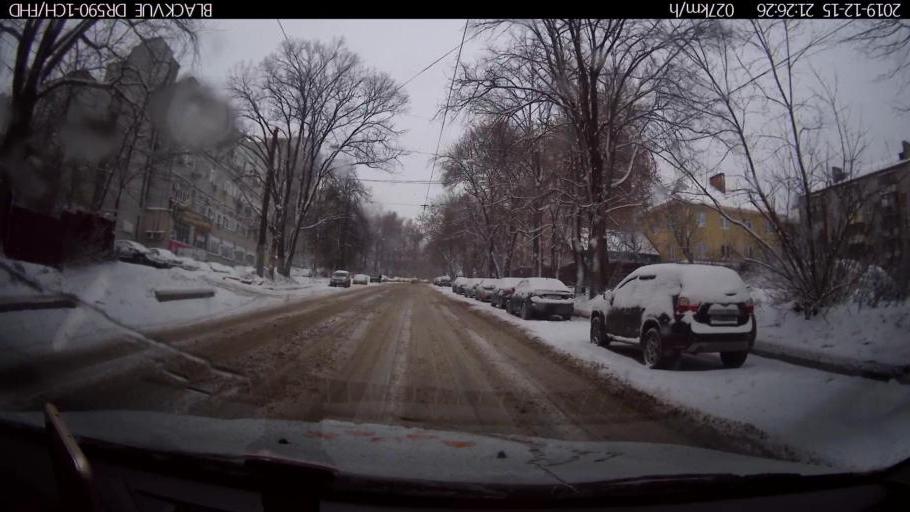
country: RU
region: Nizjnij Novgorod
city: Nizhniy Novgorod
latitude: 56.3075
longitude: 44.0188
